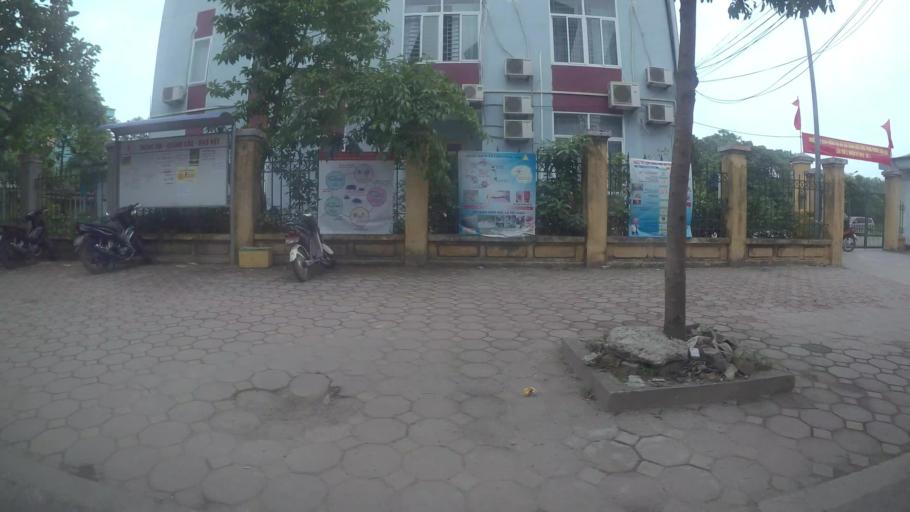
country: VN
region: Ha Noi
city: Tay Ho
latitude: 21.0733
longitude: 105.7890
